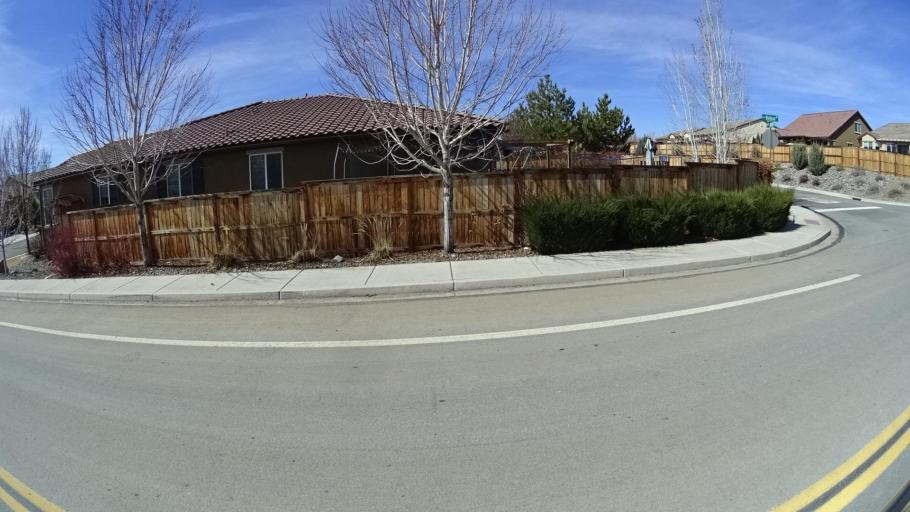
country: US
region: Nevada
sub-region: Washoe County
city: Spanish Springs
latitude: 39.5817
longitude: -119.6887
